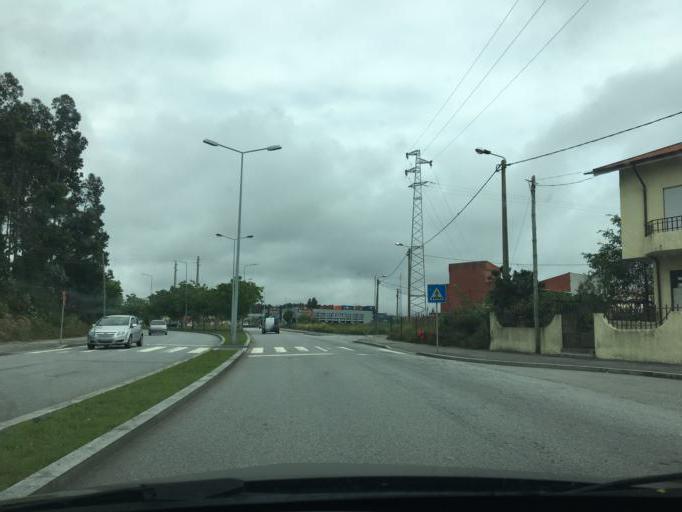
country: PT
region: Porto
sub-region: Matosinhos
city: Santa Cruz do Bispo
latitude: 41.2083
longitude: -8.6845
